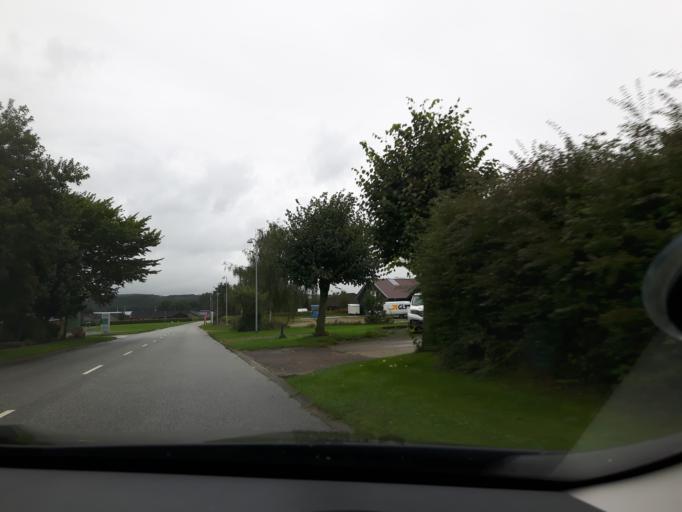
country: DK
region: Central Jutland
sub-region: Skanderborg Kommune
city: Ry
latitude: 56.1516
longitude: 9.8164
